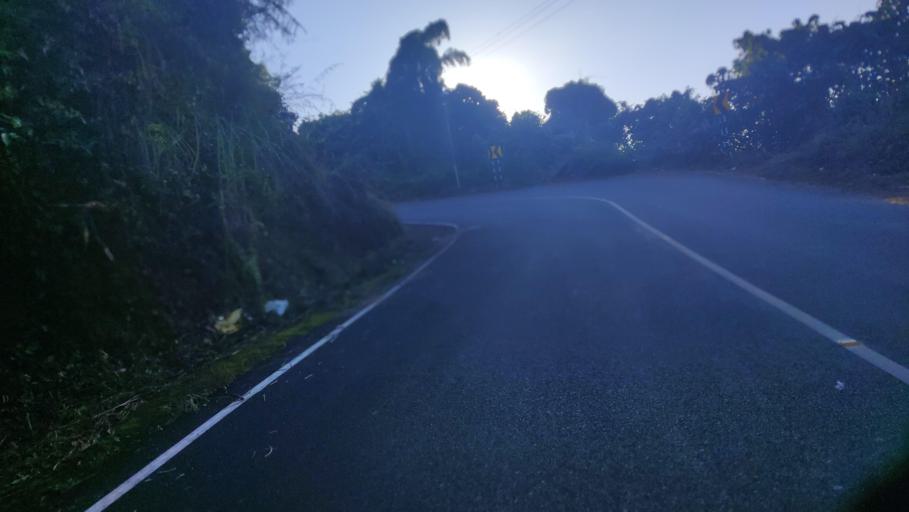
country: IN
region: Kerala
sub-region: Kasaragod District
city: Kasaragod
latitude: 12.4597
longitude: 75.0900
